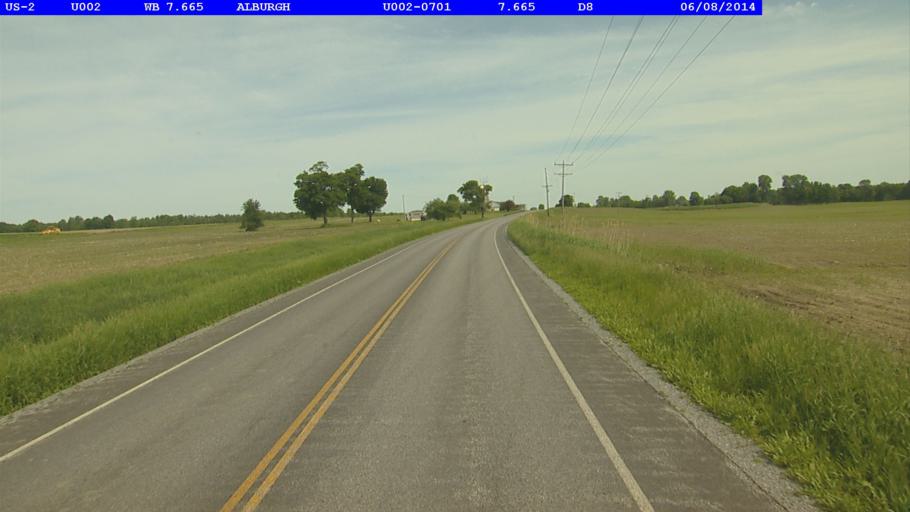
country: US
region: New York
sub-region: Clinton County
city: Rouses Point
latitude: 44.9405
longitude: -73.2748
